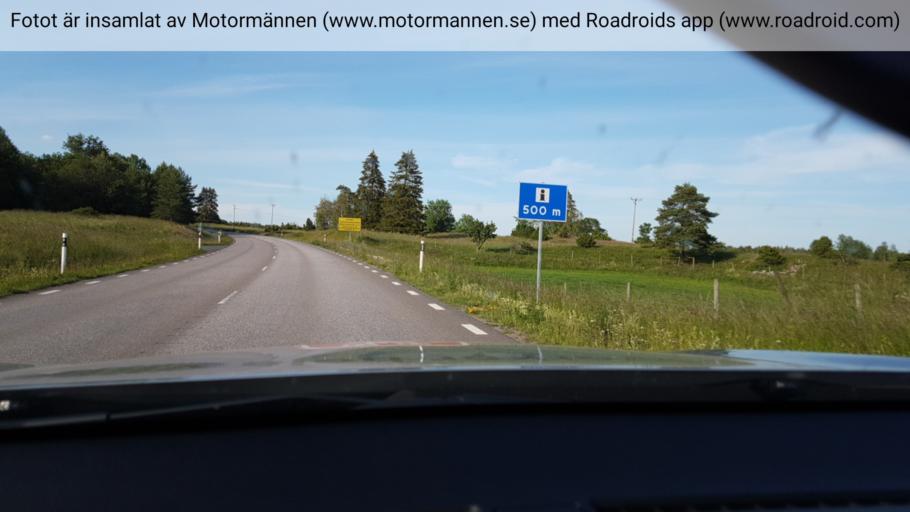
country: SE
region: Vaestra Goetaland
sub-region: Falkopings Kommun
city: Falkoeping
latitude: 58.0104
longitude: 13.5696
